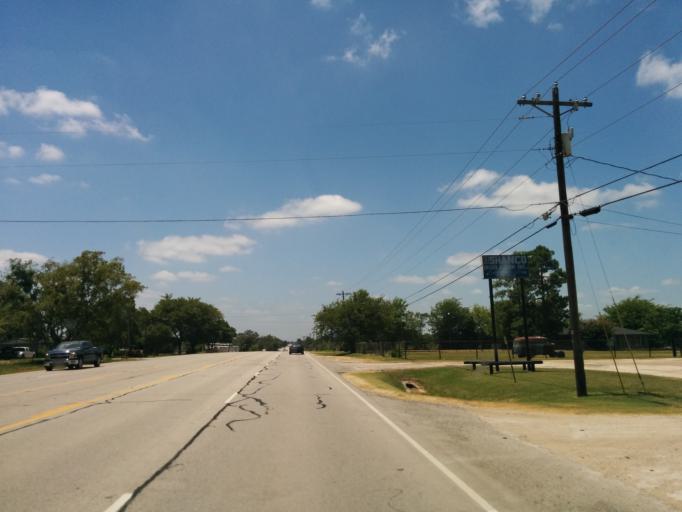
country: US
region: Texas
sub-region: Brazos County
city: Bryan
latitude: 30.7158
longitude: -96.3417
